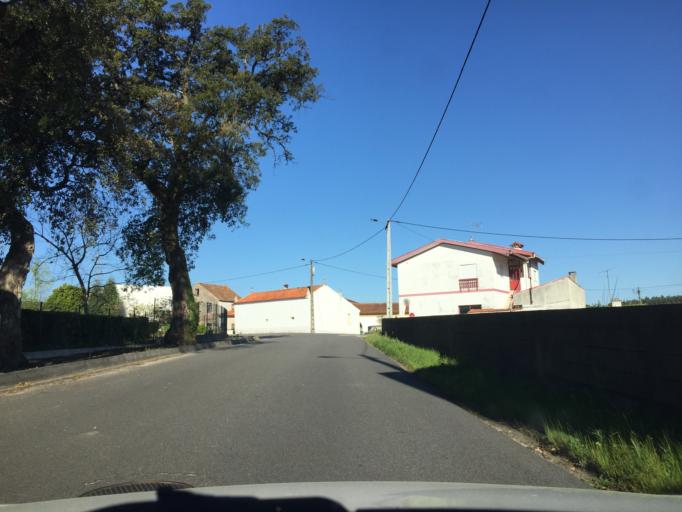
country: PT
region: Aveiro
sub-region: Anadia
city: Sangalhos
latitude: 40.4524
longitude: -8.4772
